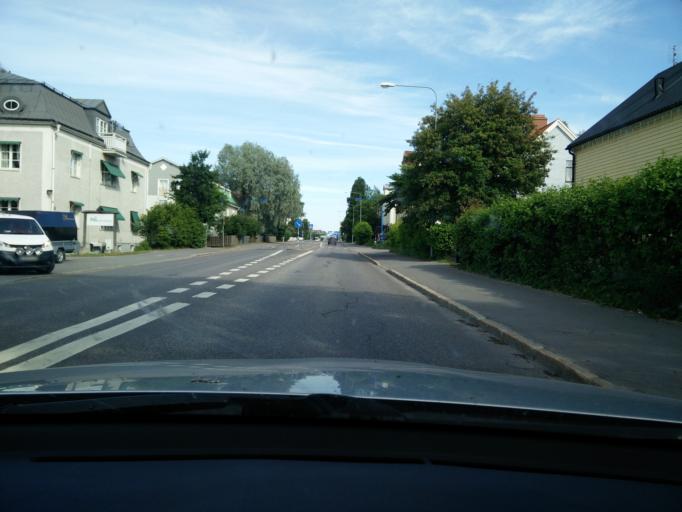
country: SE
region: Vaesternorrland
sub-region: Sundsvalls Kommun
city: Sundsvall
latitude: 62.3879
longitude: 17.2891
